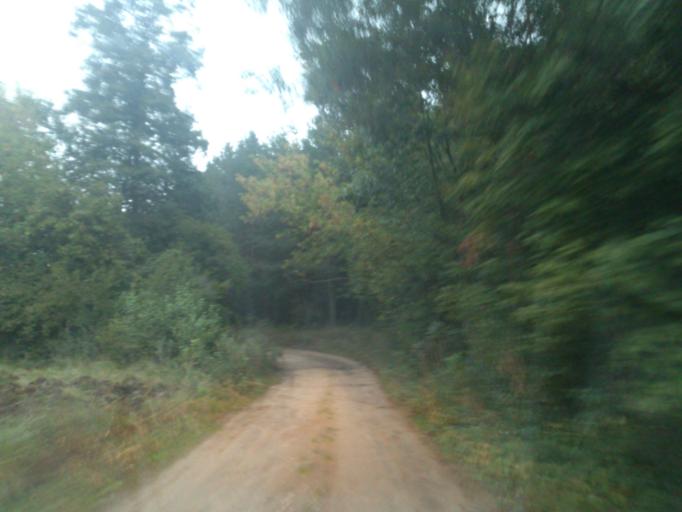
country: PL
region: Kujawsko-Pomorskie
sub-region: Powiat golubsko-dobrzynski
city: Golub-Dobrzyn
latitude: 53.1252
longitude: 19.1204
